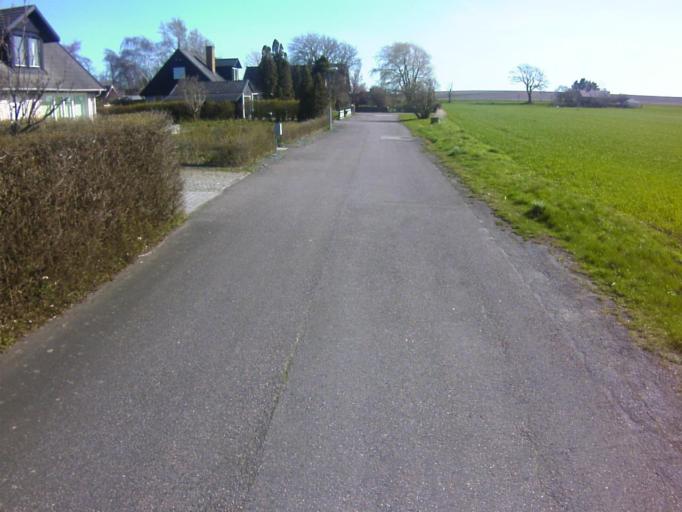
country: SE
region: Skane
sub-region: Kavlinge Kommun
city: Hofterup
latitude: 55.7689
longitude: 12.9539
